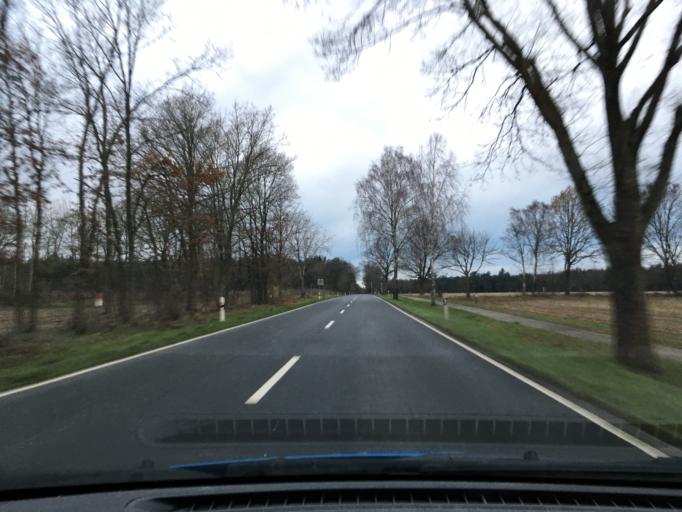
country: DE
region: Lower Saxony
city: Eimke
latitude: 52.9720
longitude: 10.2737
